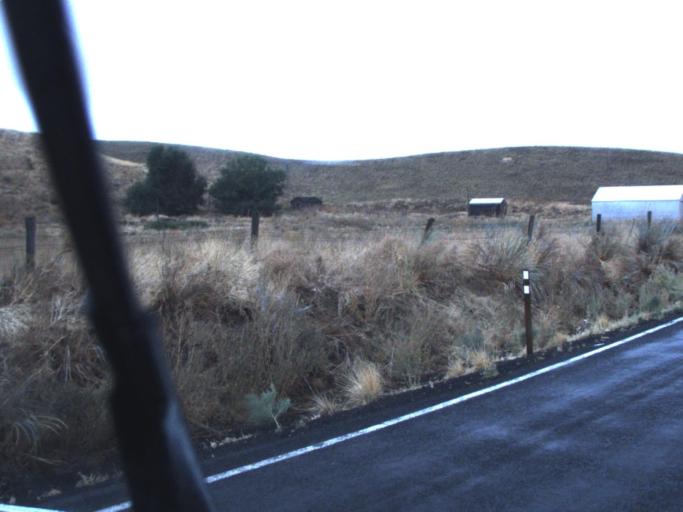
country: US
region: Washington
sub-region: Spokane County
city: Cheney
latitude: 47.1506
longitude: -117.8398
